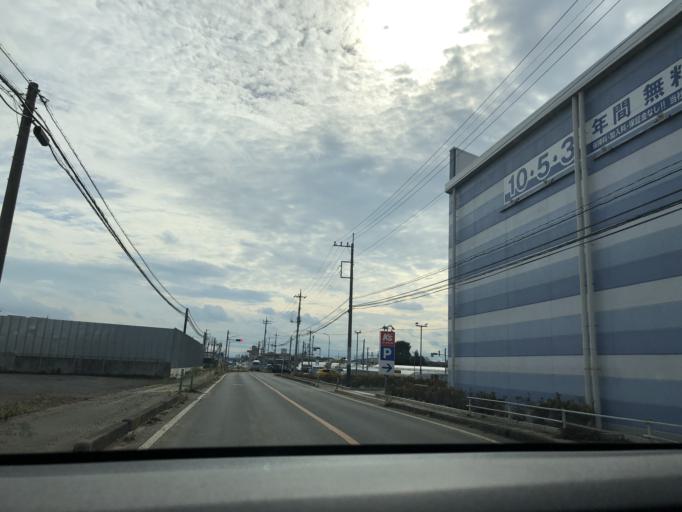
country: JP
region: Tochigi
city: Sano
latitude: 36.2971
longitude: 139.5677
